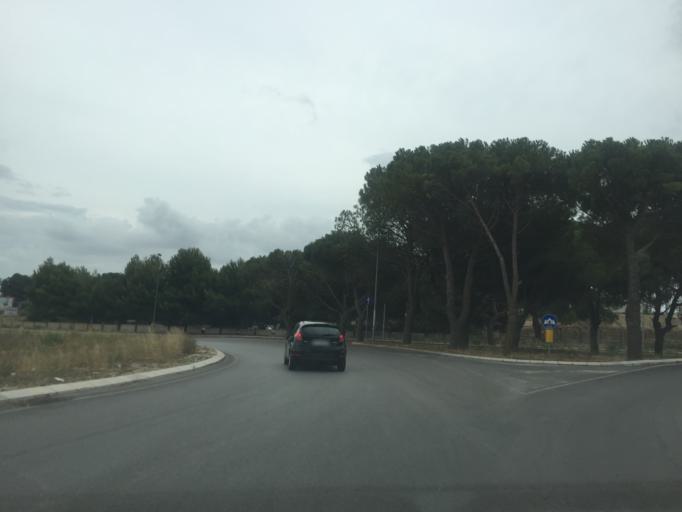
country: IT
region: Sicily
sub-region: Ragusa
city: Ragusa
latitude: 36.9003
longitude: 14.7065
